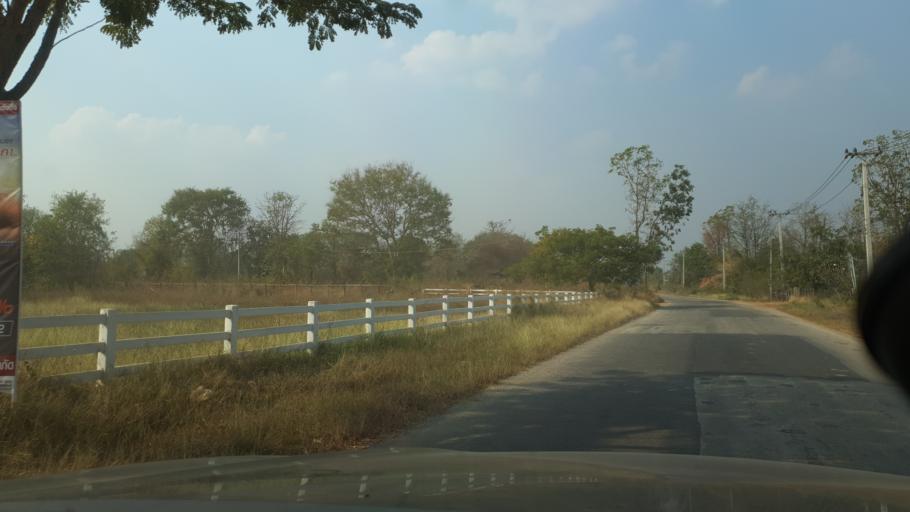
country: TH
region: Sukhothai
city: Ban Dan Lan Hoi
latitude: 17.1022
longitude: 99.5529
